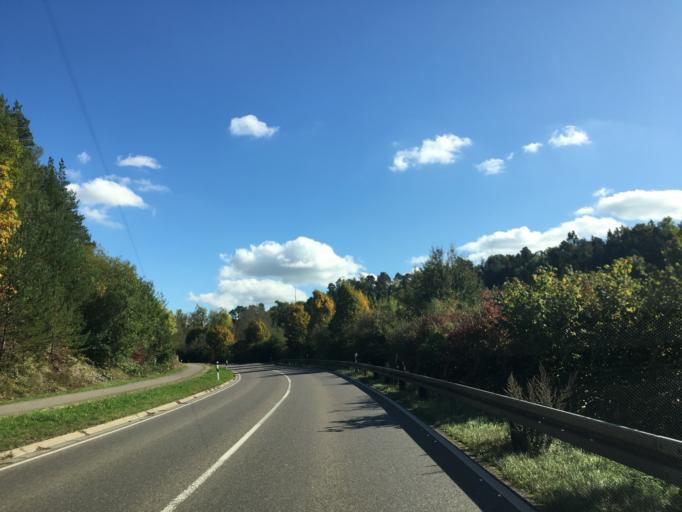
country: DE
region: Baden-Wuerttemberg
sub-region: Regierungsbezirk Stuttgart
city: Aidlingen
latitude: 48.6999
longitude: 8.9223
